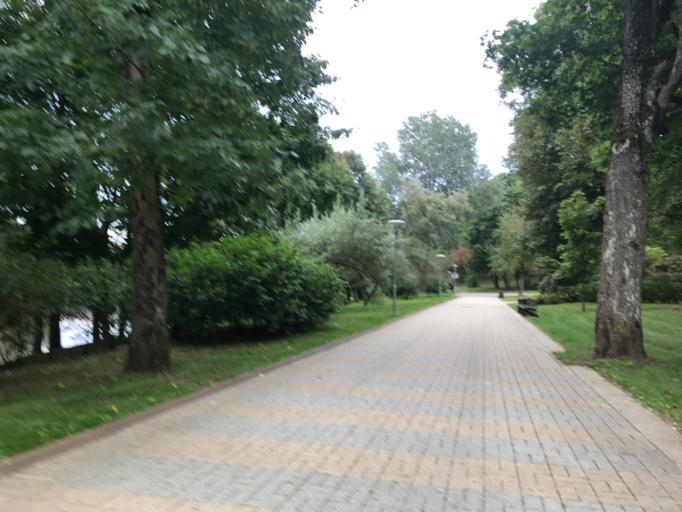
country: LT
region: Alytaus apskritis
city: Druskininkai
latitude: 54.0209
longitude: 23.9781
